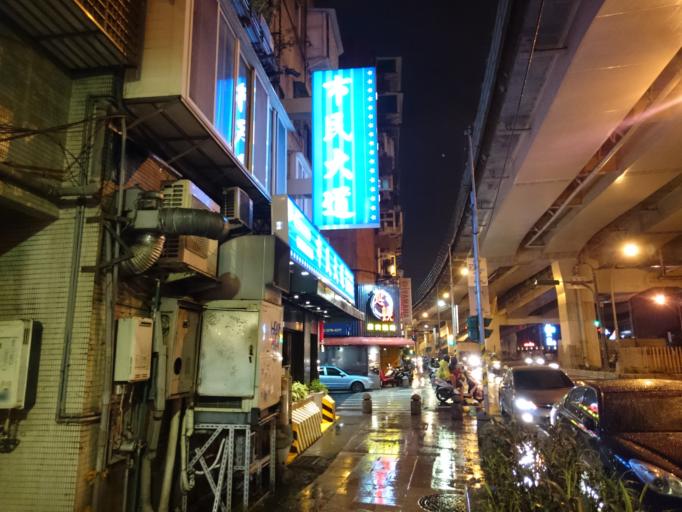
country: TW
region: Taipei
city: Taipei
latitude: 25.0444
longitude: 121.5534
